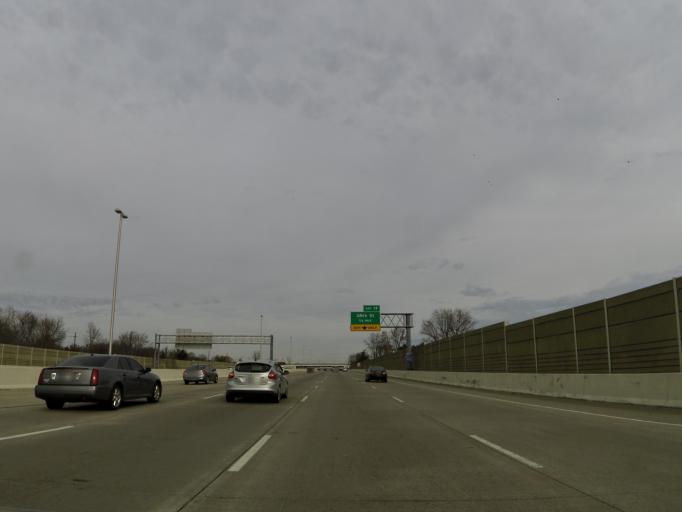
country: US
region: Indiana
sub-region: Marion County
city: Speedway
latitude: 39.8105
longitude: -86.2753
